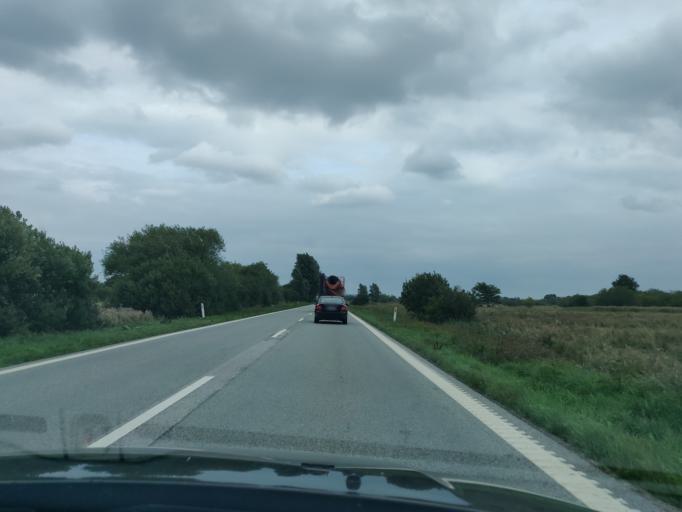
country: DK
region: North Denmark
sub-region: Alborg Kommune
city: Frejlev
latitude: 57.0140
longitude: 9.8260
